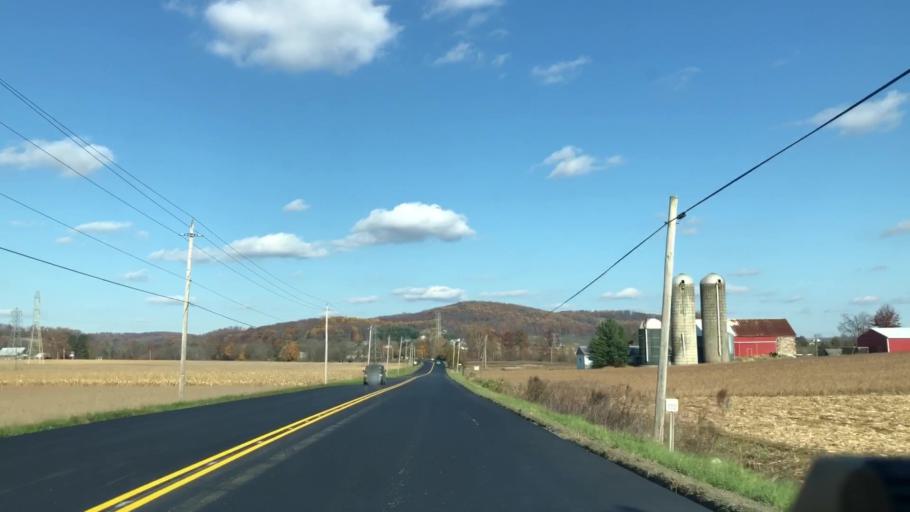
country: US
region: Pennsylvania
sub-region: Berks County
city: Bally
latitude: 40.4370
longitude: -75.5596
